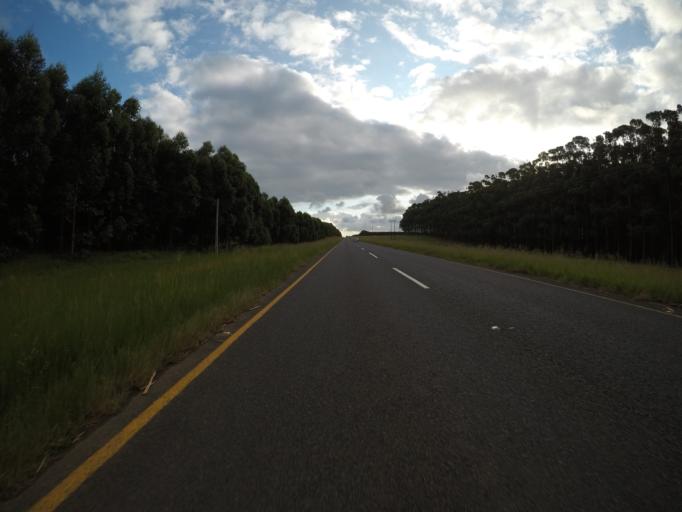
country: ZA
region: KwaZulu-Natal
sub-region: uMkhanyakude District Municipality
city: Mtubatuba
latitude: -28.3878
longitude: 32.2329
